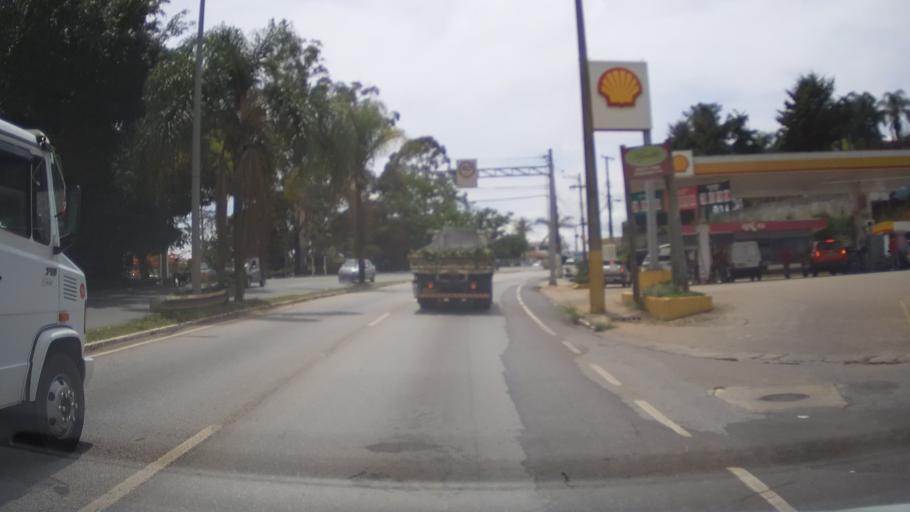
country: BR
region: Minas Gerais
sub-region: Nova Lima
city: Nova Lima
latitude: -19.9989
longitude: -43.8938
